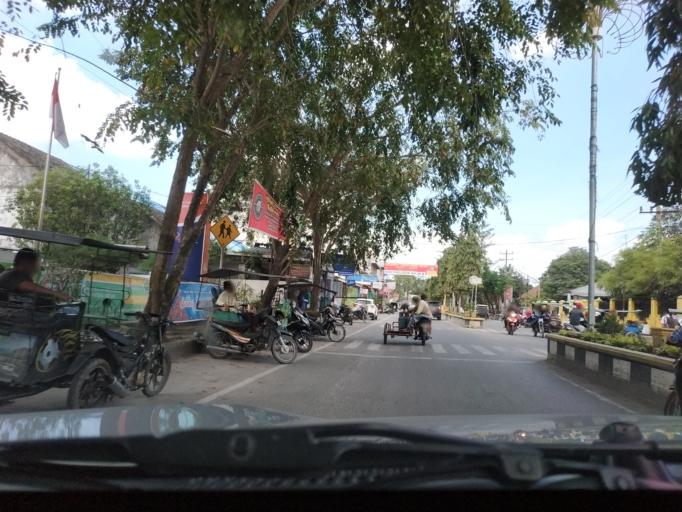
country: ID
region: North Sumatra
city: Tanjungbalai
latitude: 2.9616
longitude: 99.8028
